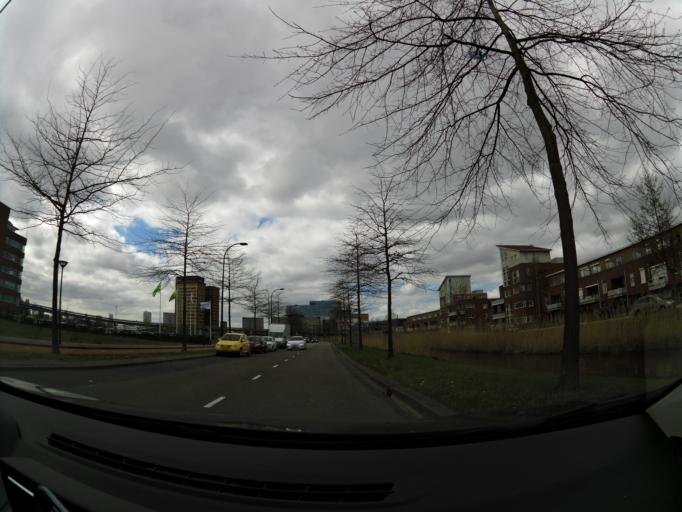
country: NL
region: South Holland
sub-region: Gemeente Rotterdam
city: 's-Gravenland
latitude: 51.9159
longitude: 4.5429
